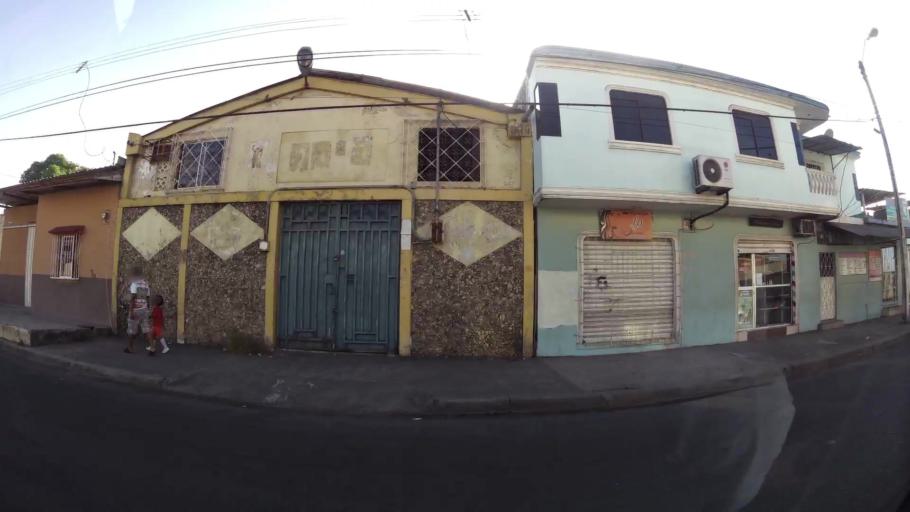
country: EC
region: Guayas
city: Guayaquil
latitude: -2.2272
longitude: -79.9061
